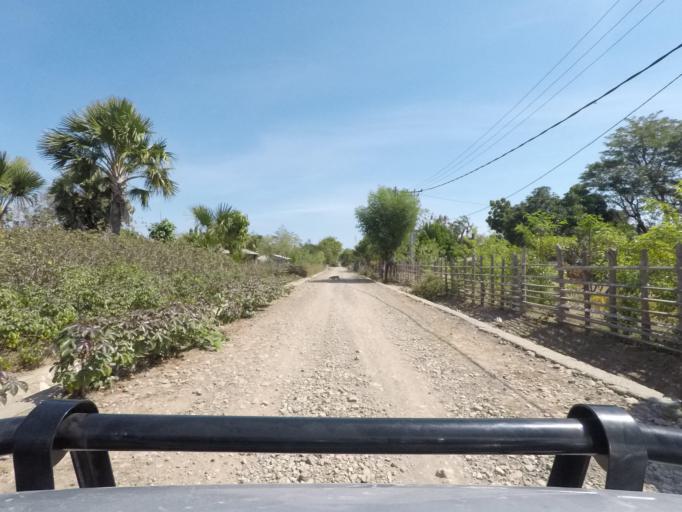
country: TL
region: Liquica
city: Maubara
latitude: -8.7812
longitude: 125.1050
